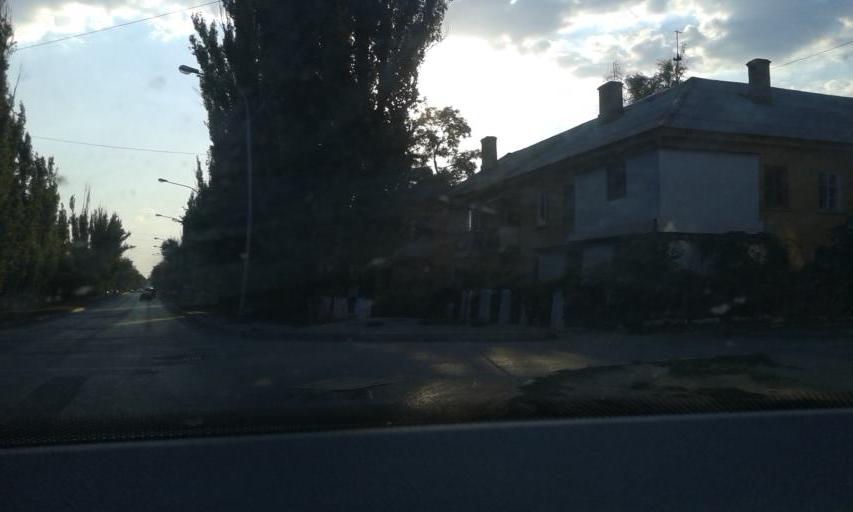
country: RU
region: Volgograd
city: Volgograd
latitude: 48.6618
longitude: 44.4484
